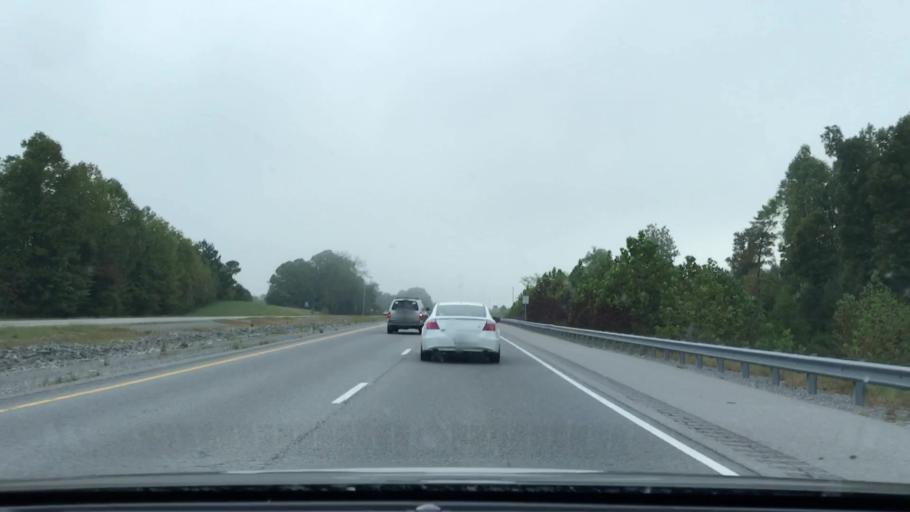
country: US
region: Tennessee
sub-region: Sumner County
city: Portland
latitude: 36.4872
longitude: -86.4867
